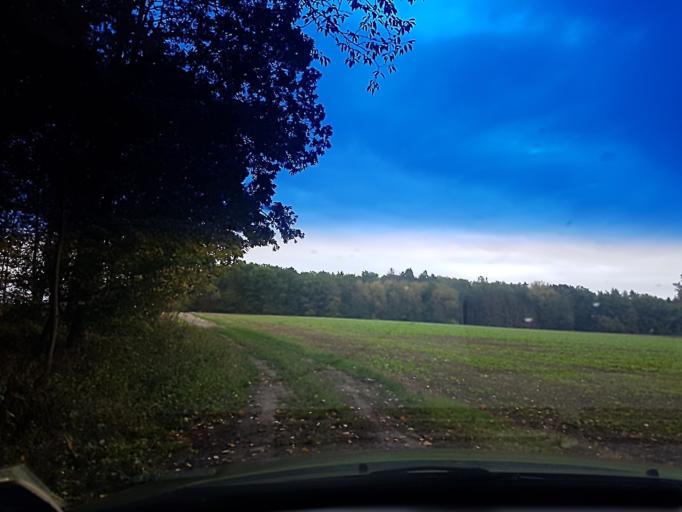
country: DE
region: Bavaria
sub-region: Upper Franconia
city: Memmelsdorf
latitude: 49.9721
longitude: 10.9527
